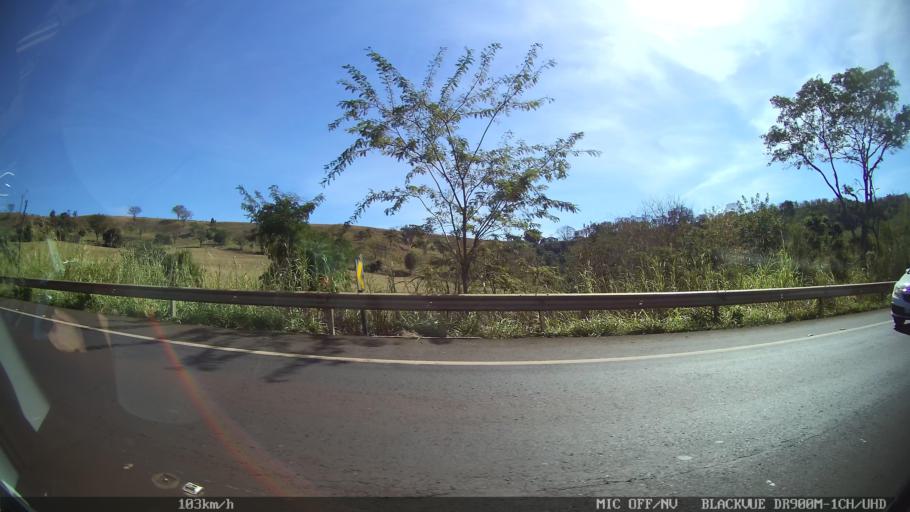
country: BR
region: Sao Paulo
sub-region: Sao Joaquim Da Barra
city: Sao Joaquim da Barra
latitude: -20.5539
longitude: -47.6799
